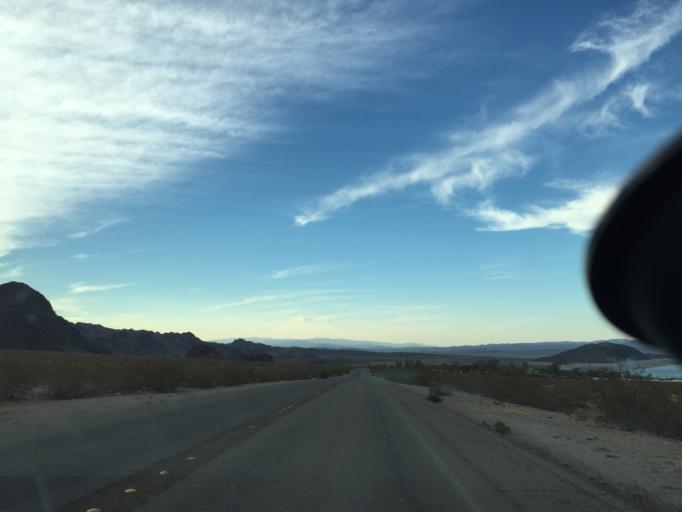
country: US
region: Nevada
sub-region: Clark County
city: Boulder City
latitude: 36.0271
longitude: -114.7993
